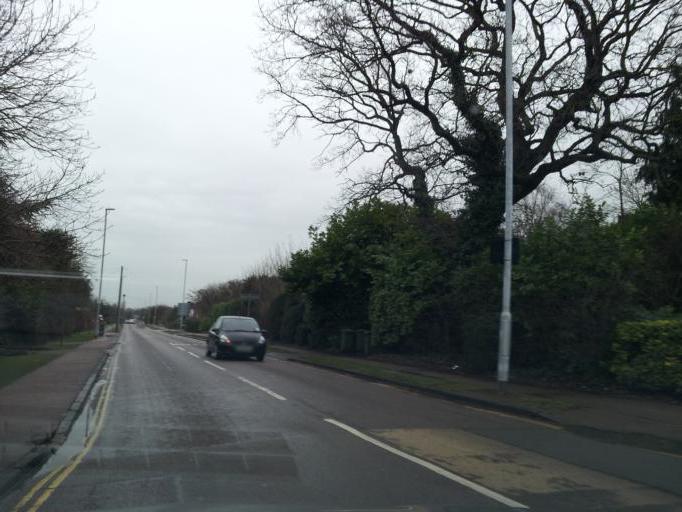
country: GB
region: England
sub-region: Cambridgeshire
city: Cambridge
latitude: 52.1793
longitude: 0.1492
